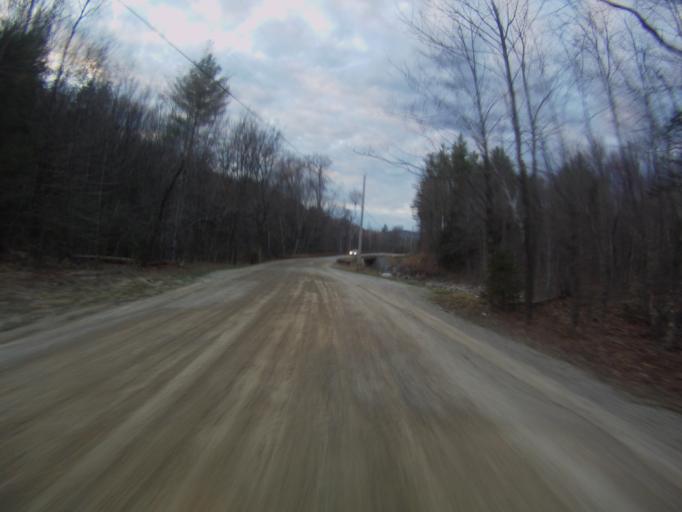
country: US
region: Vermont
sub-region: Addison County
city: Middlebury (village)
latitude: 43.9629
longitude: -73.0289
